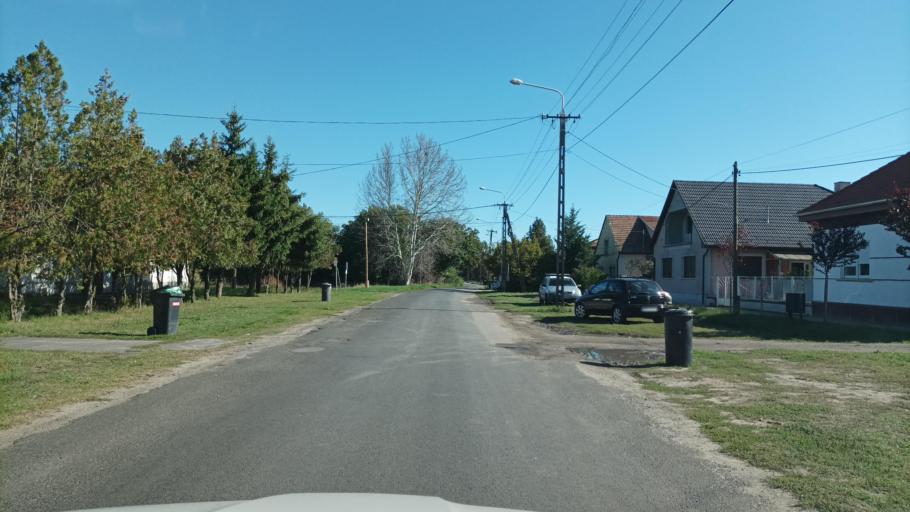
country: HU
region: Pest
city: Cegledbercel
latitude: 47.2183
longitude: 19.6602
